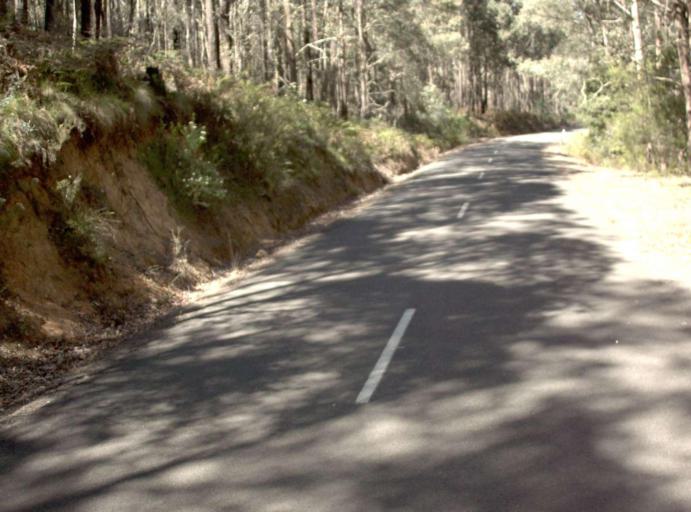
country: AU
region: New South Wales
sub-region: Bombala
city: Bombala
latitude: -37.0857
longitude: 148.7725
